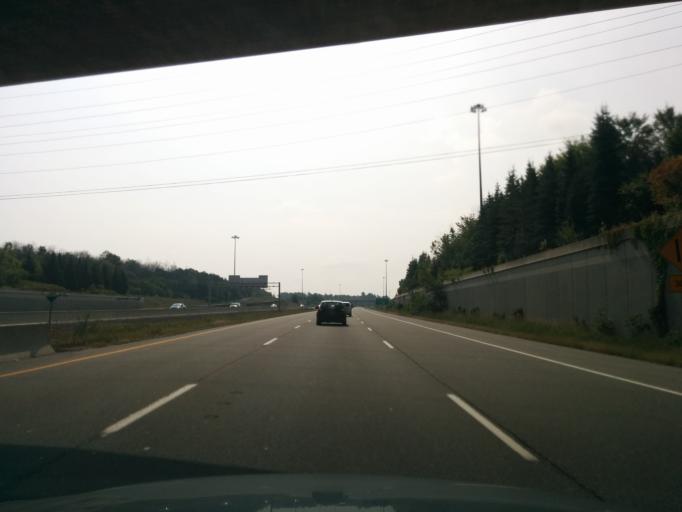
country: CA
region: Ontario
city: Bells Corners
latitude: 45.3316
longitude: -75.8097
